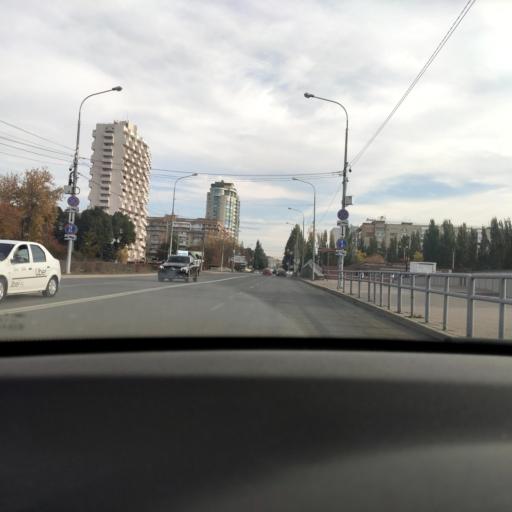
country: RU
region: Samara
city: Samara
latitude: 53.2090
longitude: 50.1339
